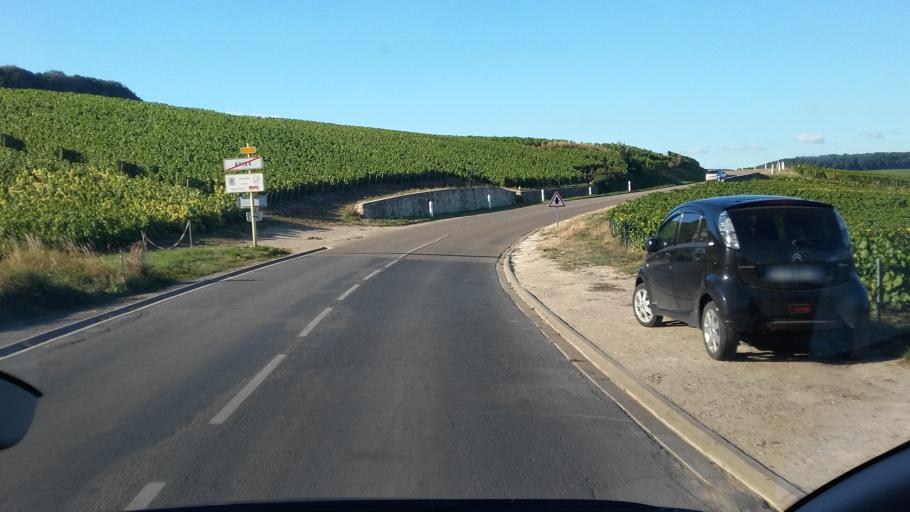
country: FR
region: Champagne-Ardenne
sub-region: Departement de la Marne
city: Avize
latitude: 48.9732
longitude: 4.0032
